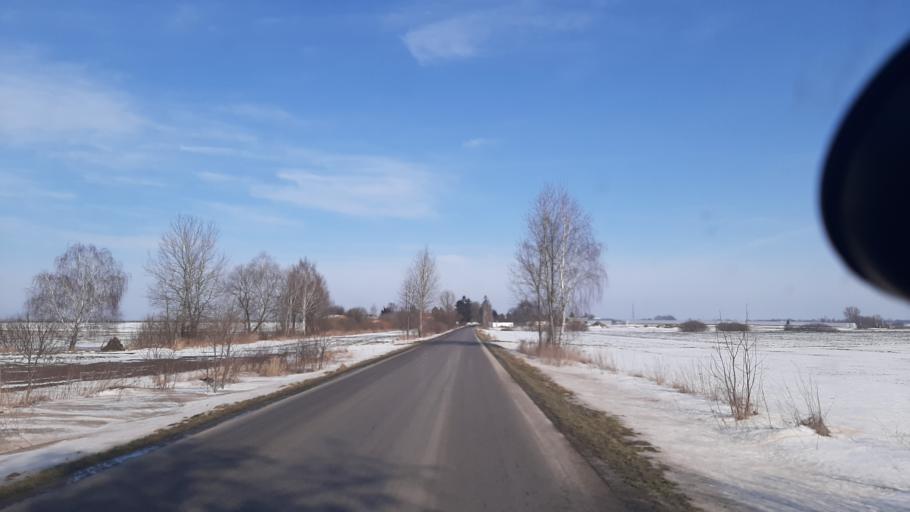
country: PL
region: Lublin Voivodeship
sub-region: Powiat pulawski
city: Kurow
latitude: 51.3729
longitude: 22.1511
